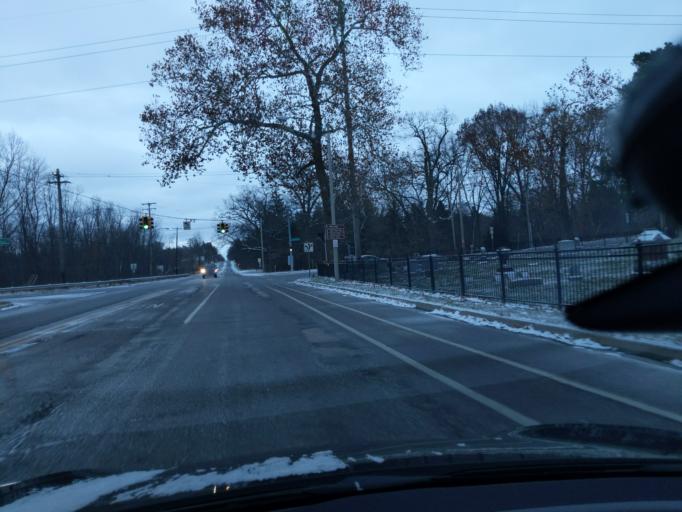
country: US
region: Michigan
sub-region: Ingham County
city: Lansing
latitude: 42.7119
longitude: -84.5240
